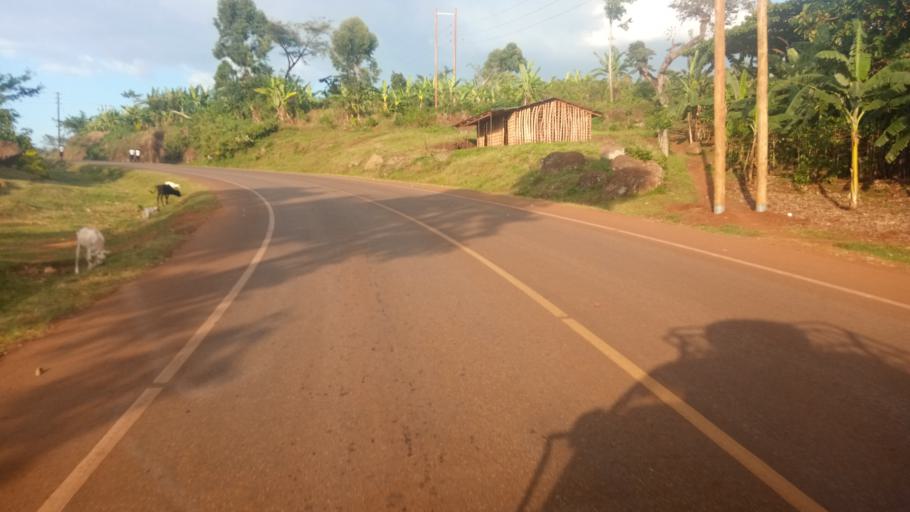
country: UG
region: Eastern Region
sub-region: Sironko District
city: Sironko
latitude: 1.3198
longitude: 34.3428
